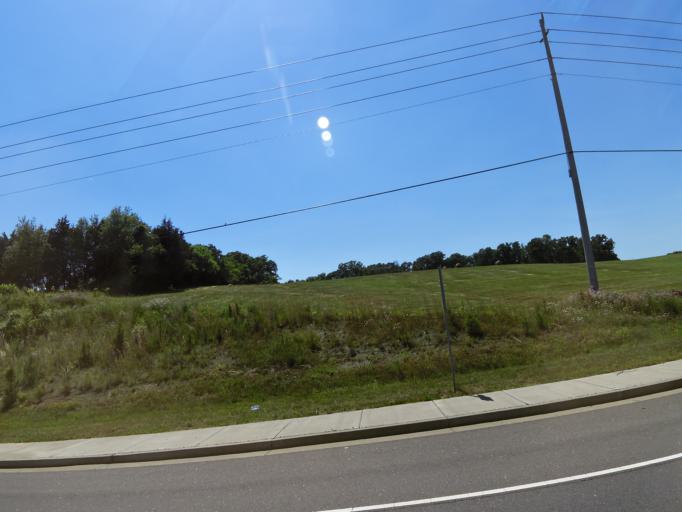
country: US
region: Tennessee
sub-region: Sevier County
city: Sevierville
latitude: 35.9607
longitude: -83.5941
